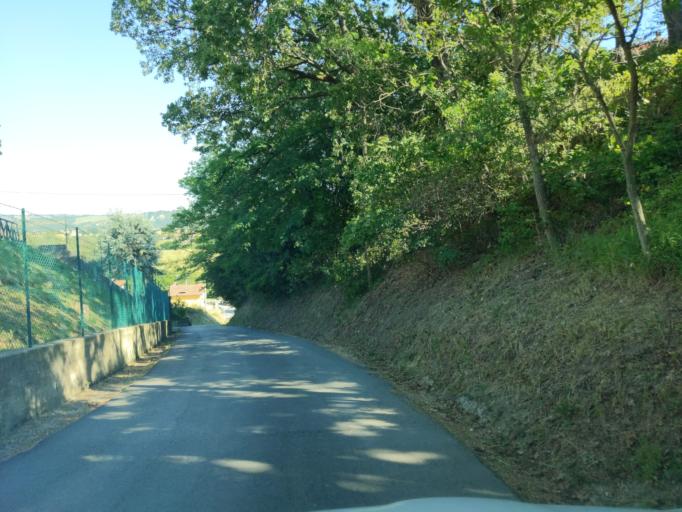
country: IT
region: The Marches
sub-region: Provincia di Pesaro e Urbino
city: Cuccurano
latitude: 43.7982
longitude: 12.9596
